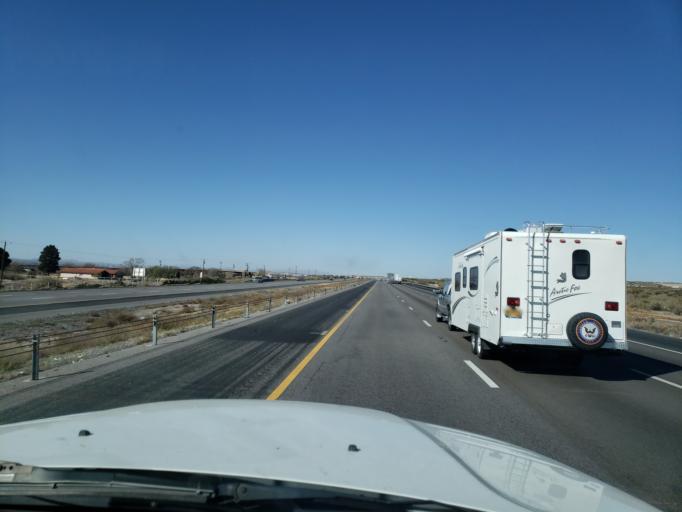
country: US
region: New Mexico
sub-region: Dona Ana County
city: Mesquite
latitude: 32.1641
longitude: -106.6626
